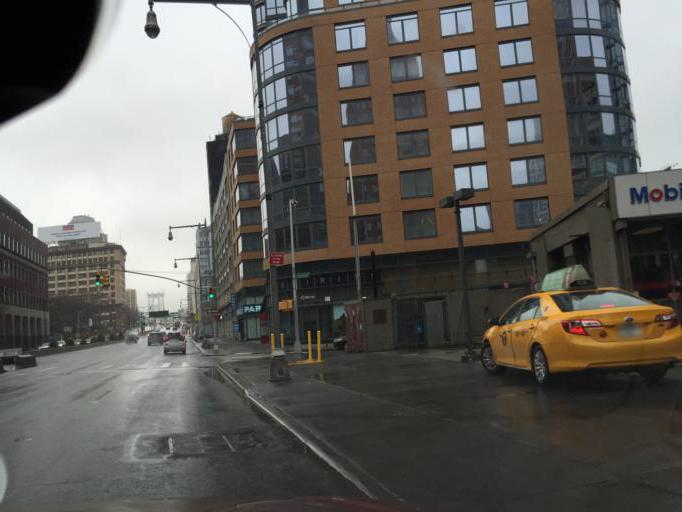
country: US
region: New York
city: New York City
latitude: 40.6946
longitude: -73.9836
